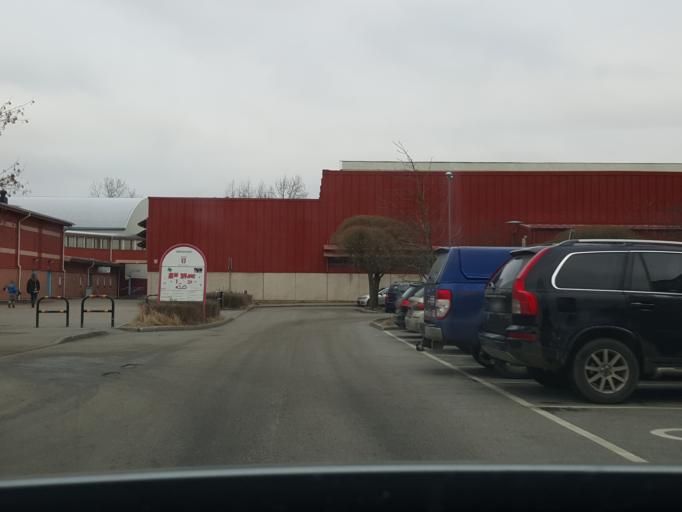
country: SE
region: Stockholm
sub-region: Botkyrka Kommun
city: Tumba
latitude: 59.2012
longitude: 17.8332
